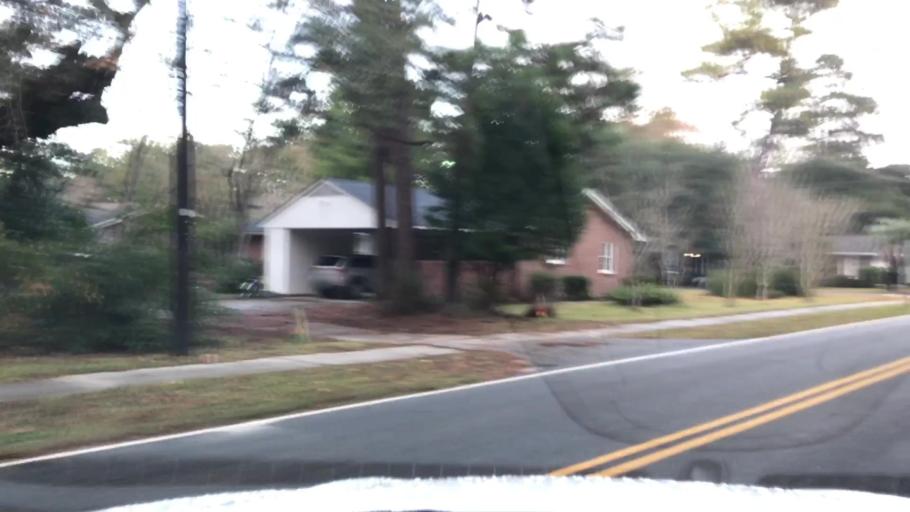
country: US
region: South Carolina
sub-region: Charleston County
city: North Charleston
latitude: 32.8176
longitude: -79.9975
